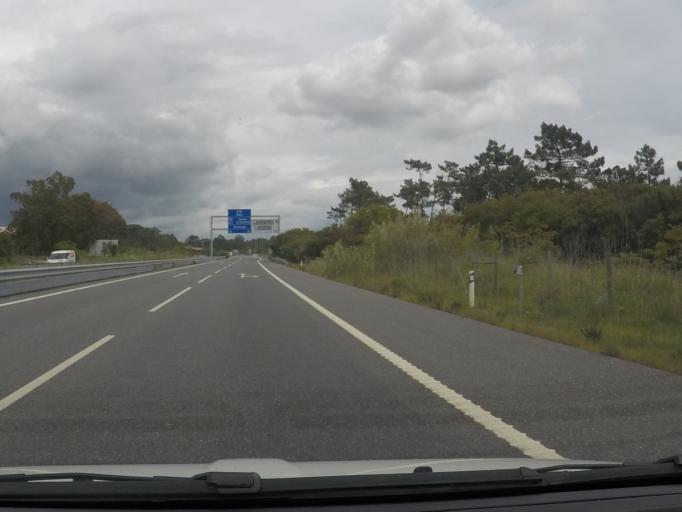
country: PT
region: Setubal
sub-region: Sines
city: Sines
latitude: 37.9735
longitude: -8.8153
